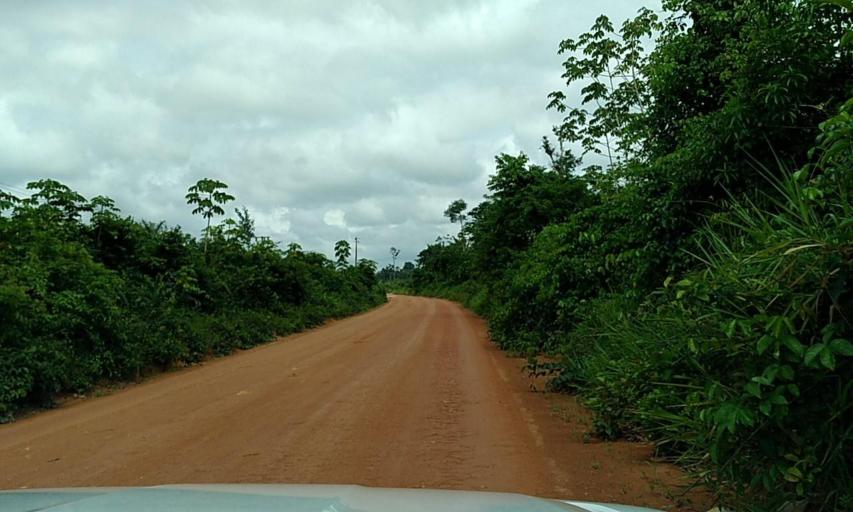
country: BR
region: Para
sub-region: Senador Jose Porfirio
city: Senador Jose Porfirio
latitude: -2.7906
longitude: -51.7637
